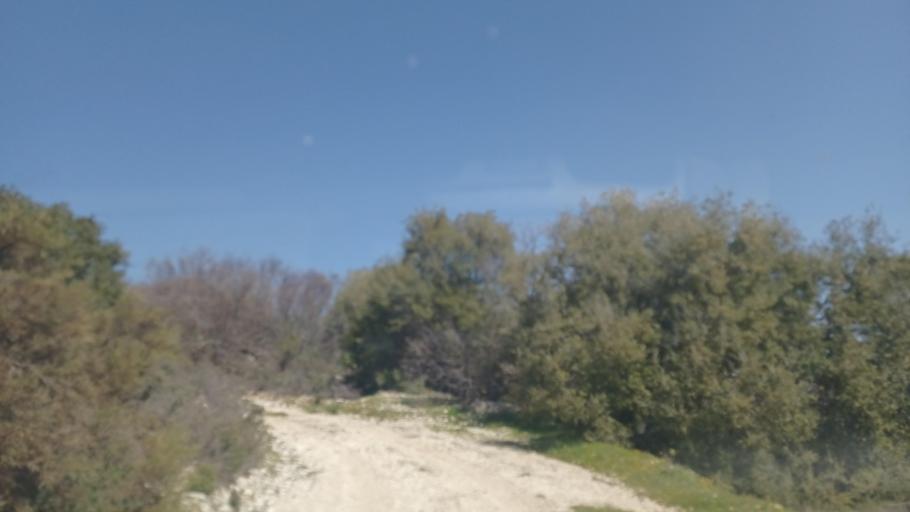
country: CY
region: Limassol
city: Pachna
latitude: 34.8703
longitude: 32.7081
